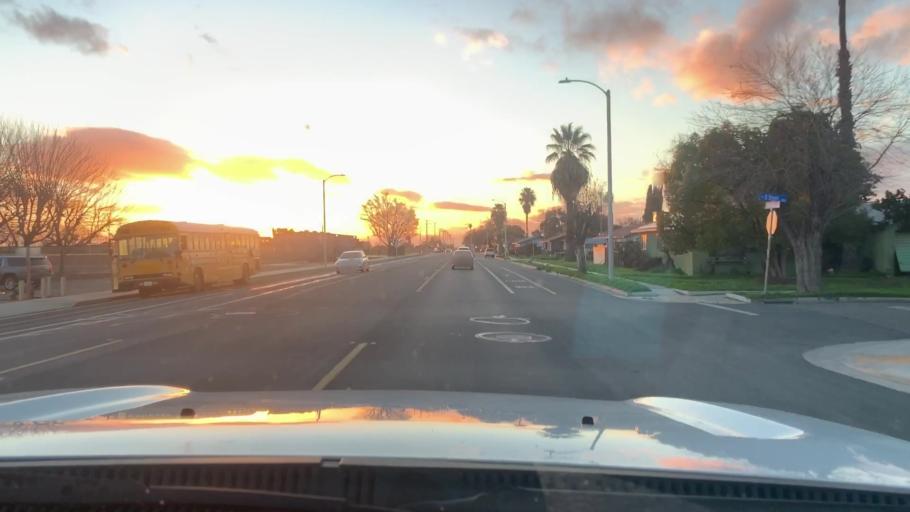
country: US
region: California
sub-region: Tulare County
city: Tulare
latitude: 36.1965
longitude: -119.3548
